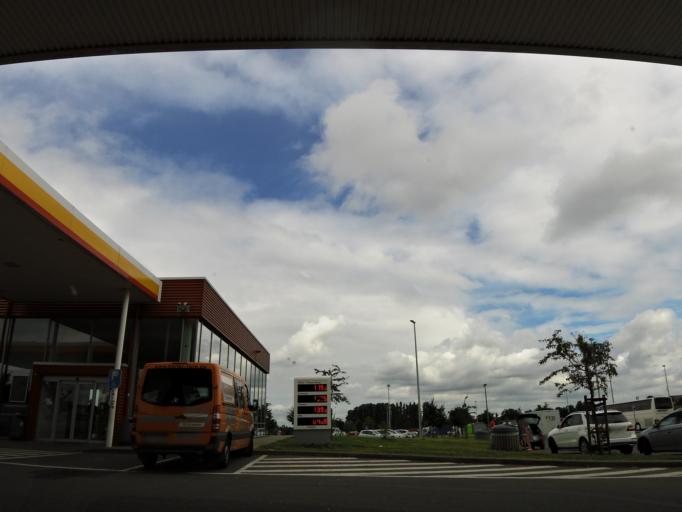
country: BE
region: Wallonia
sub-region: Province de Liege
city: Blegny
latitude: 50.6548
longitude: 5.7111
